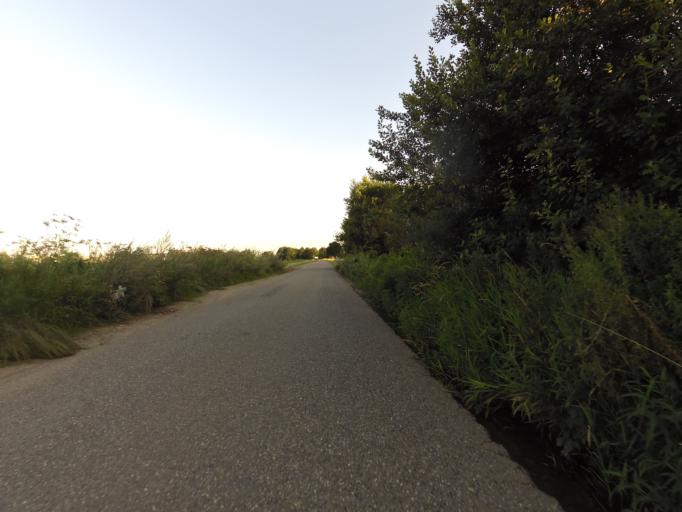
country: NL
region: Gelderland
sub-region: Gemeente Zevenaar
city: Zevenaar
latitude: 51.8771
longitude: 6.0500
